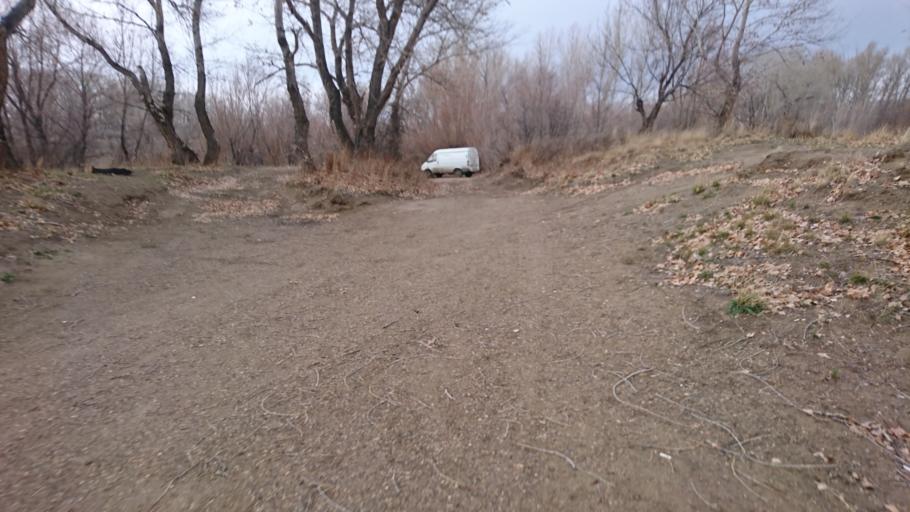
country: RU
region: Orenburg
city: Novotroitsk
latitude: 51.1650
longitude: 58.3214
